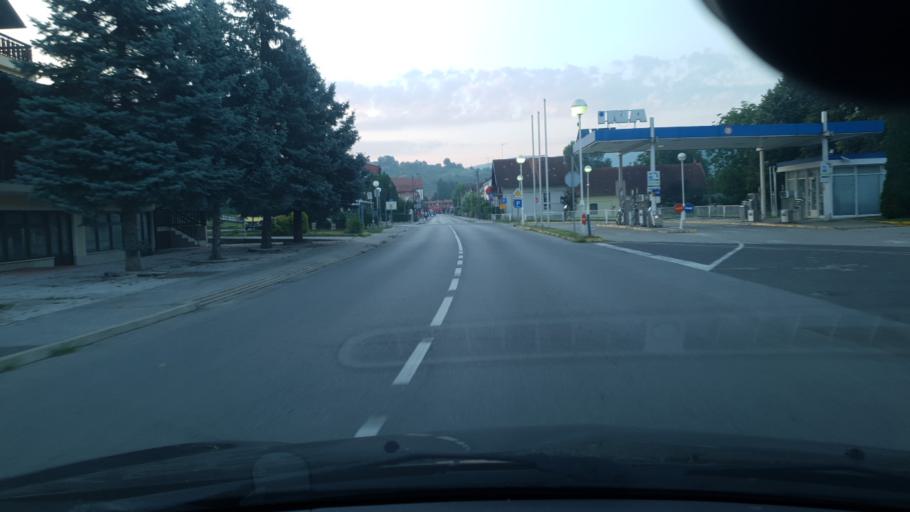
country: HR
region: Krapinsko-Zagorska
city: Marija Bistrica
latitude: 46.0052
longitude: 16.1153
